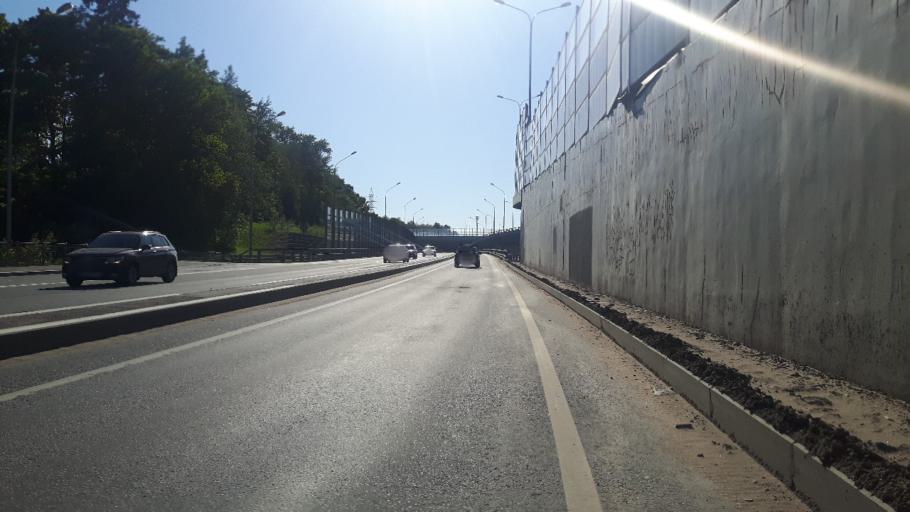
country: RU
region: St.-Petersburg
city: Bol'shaya Izhora
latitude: 59.9266
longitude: 29.6753
